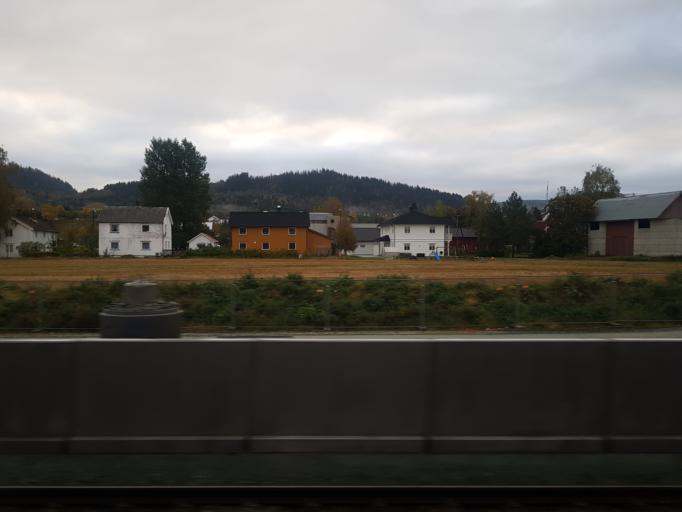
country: NO
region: Sor-Trondelag
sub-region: Melhus
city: Lundamo
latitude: 63.2044
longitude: 10.3042
